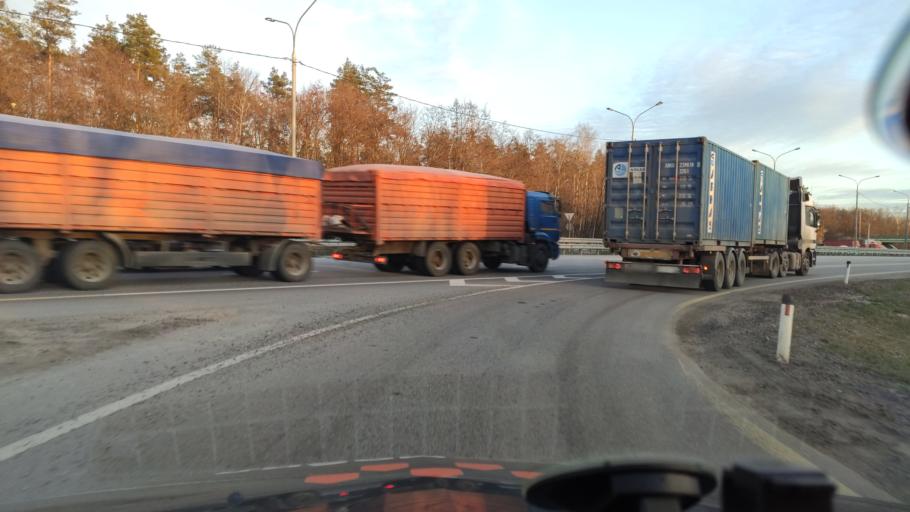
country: RU
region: Voronezj
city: Ramon'
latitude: 51.8913
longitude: 39.2176
